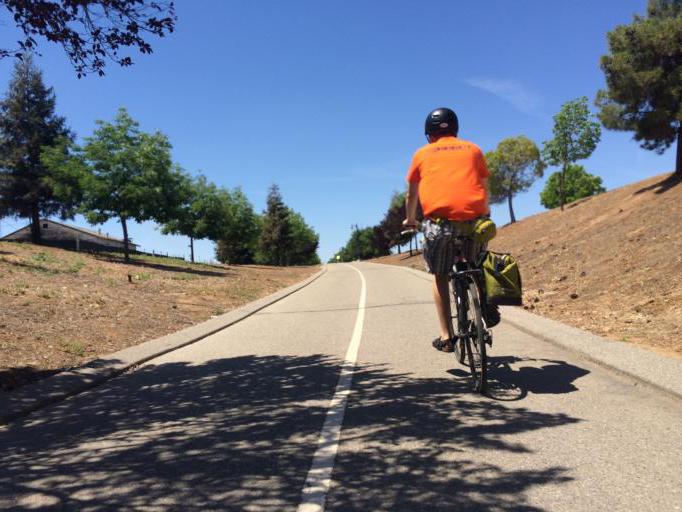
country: US
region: California
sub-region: Fresno County
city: Clovis
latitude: 36.8378
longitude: -119.7087
